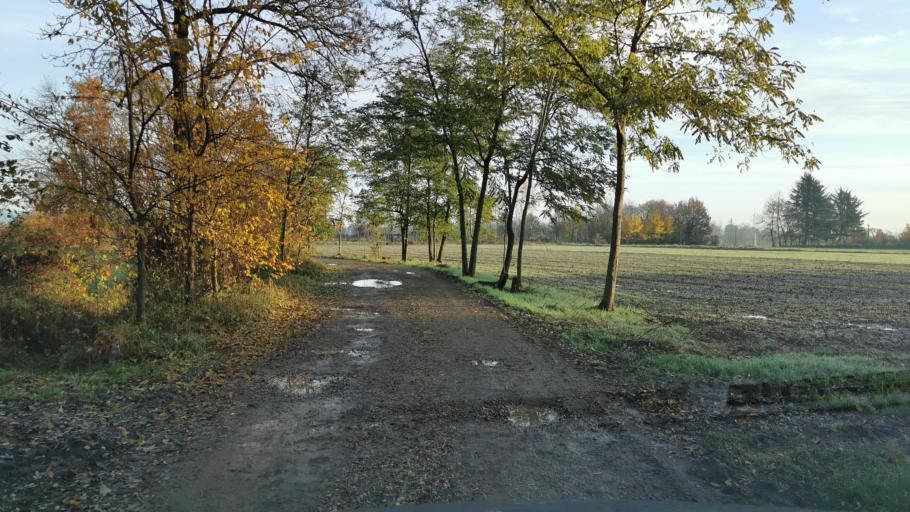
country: IT
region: Piedmont
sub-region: Provincia di Torino
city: San Francesco al Campo
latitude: 45.2058
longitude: 7.6727
